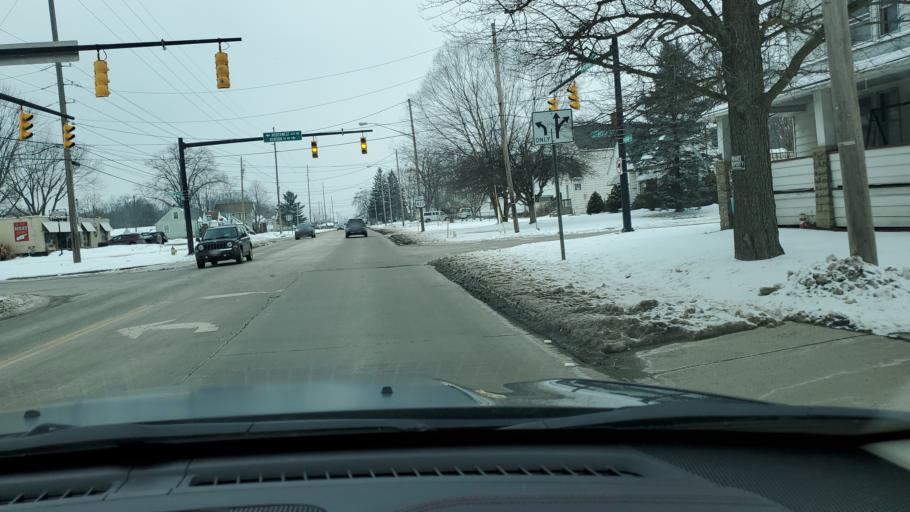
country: US
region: Ohio
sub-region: Trumbull County
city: Warren
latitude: 41.2463
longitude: -80.8457
